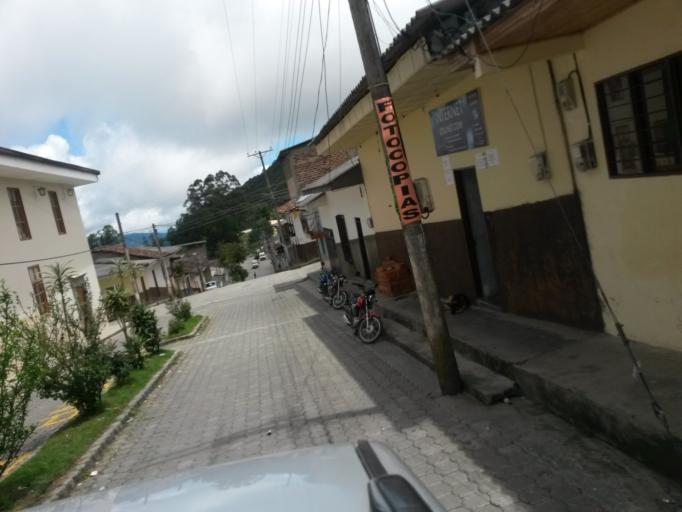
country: CO
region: Cauca
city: Almaguer
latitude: 1.9140
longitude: -76.8549
